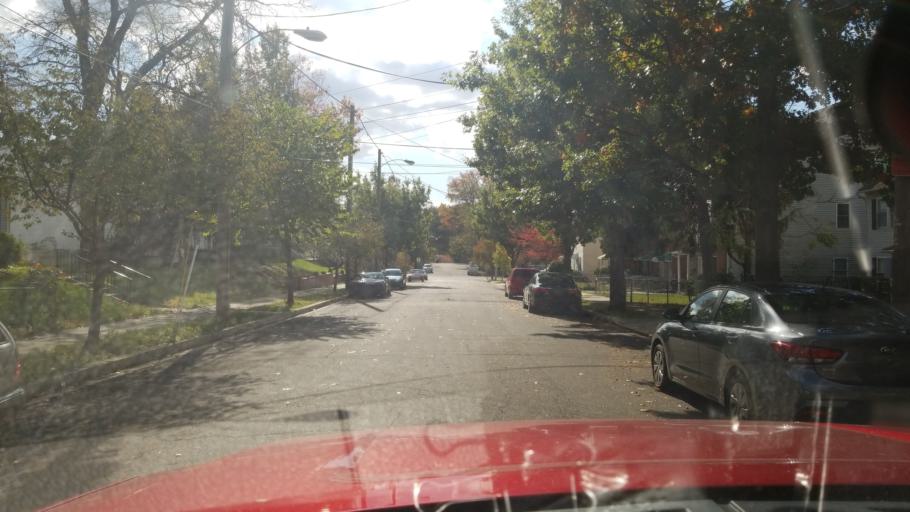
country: US
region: Maryland
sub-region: Prince George's County
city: Fairmount Heights
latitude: 38.8940
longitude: -76.9150
